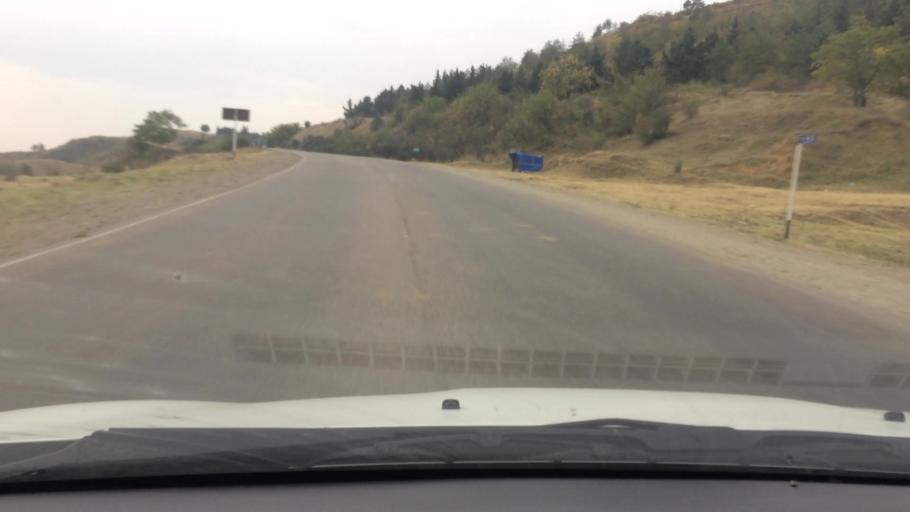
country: GE
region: T'bilisi
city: Tbilisi
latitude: 41.5997
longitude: 44.7785
